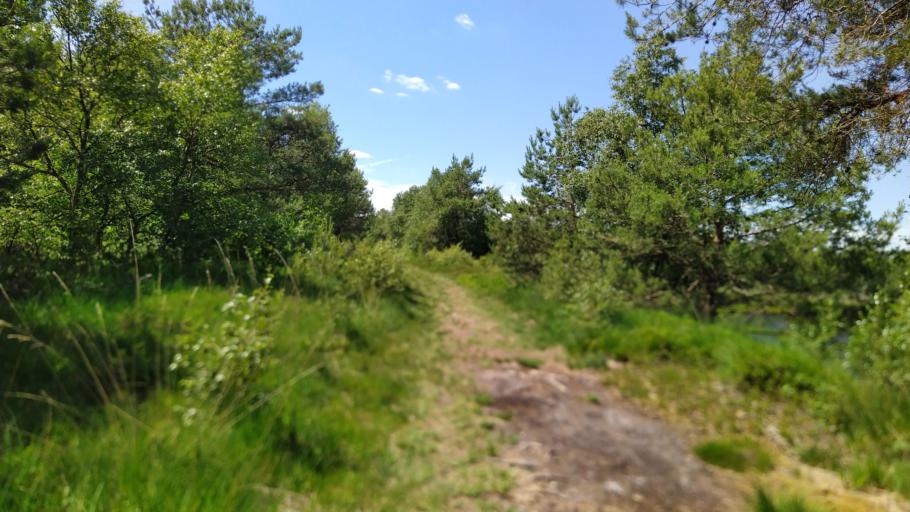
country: DE
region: Lower Saxony
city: Oldendorf
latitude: 53.5532
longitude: 9.2693
